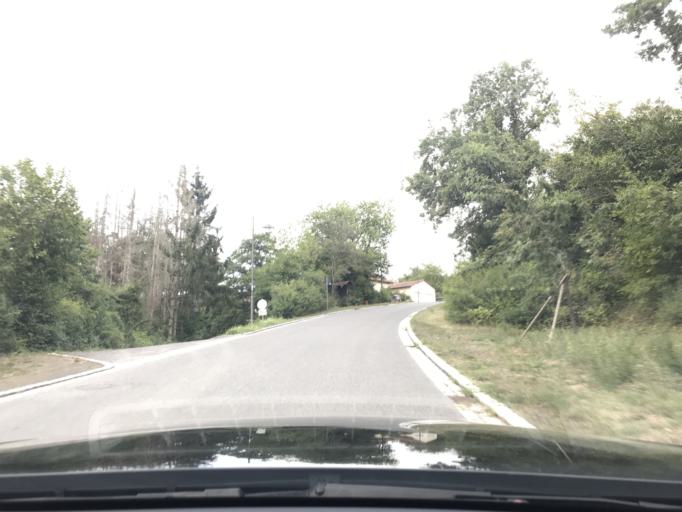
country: DE
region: Bavaria
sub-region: Regierungsbezirk Unterfranken
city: Breitbrunn
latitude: 50.0466
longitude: 10.6598
